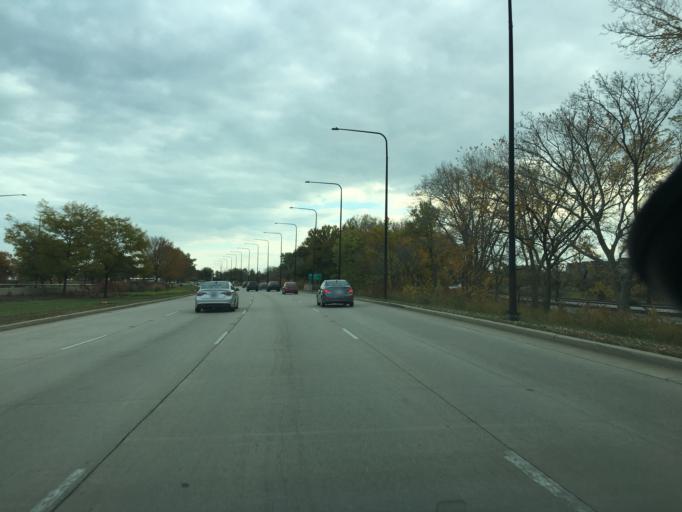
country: US
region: Illinois
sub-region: Cook County
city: Chicago
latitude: 41.8300
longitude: -87.6053
